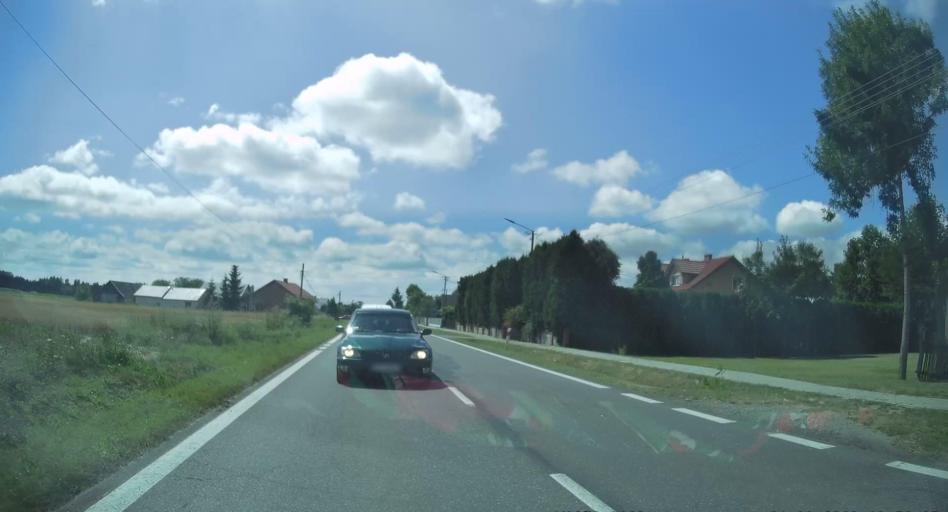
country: PL
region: Subcarpathian Voivodeship
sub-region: Powiat mielecki
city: Padew Narodowa
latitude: 50.4223
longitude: 21.4838
